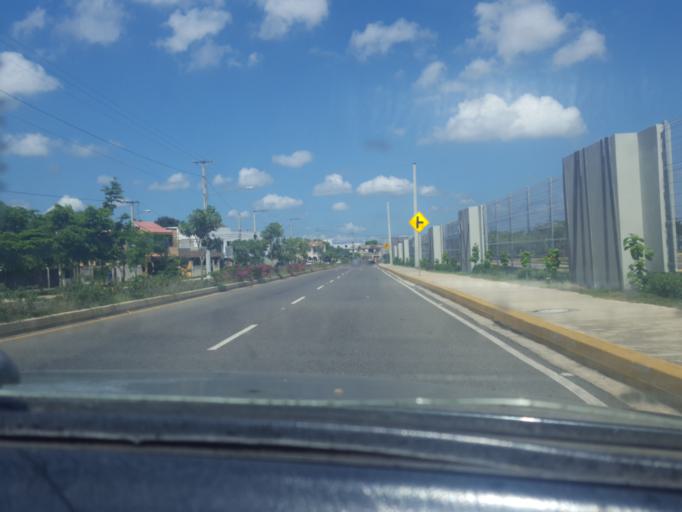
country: DO
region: Santiago
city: Santiago de los Caballeros
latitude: 19.4957
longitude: -70.6994
